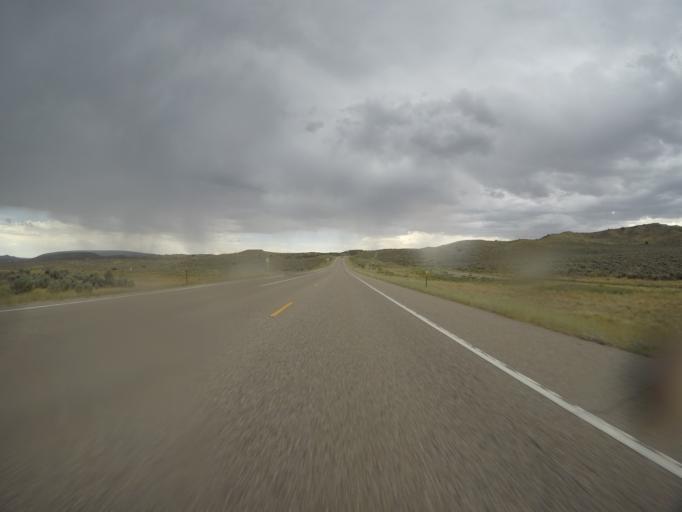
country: US
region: Colorado
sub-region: Rio Blanco County
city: Rangely
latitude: 40.4026
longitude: -108.3425
